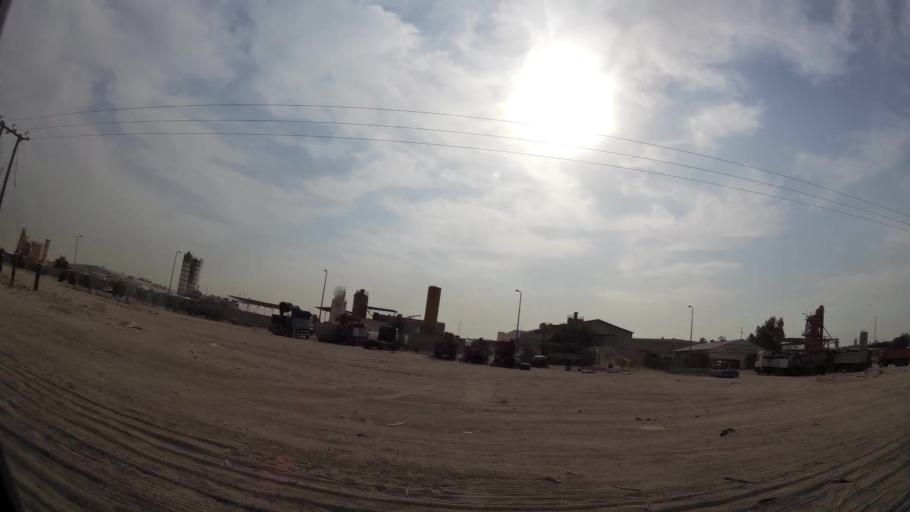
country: KW
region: Muhafazat al Jahra'
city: Al Jahra'
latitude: 29.3103
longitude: 47.7433
